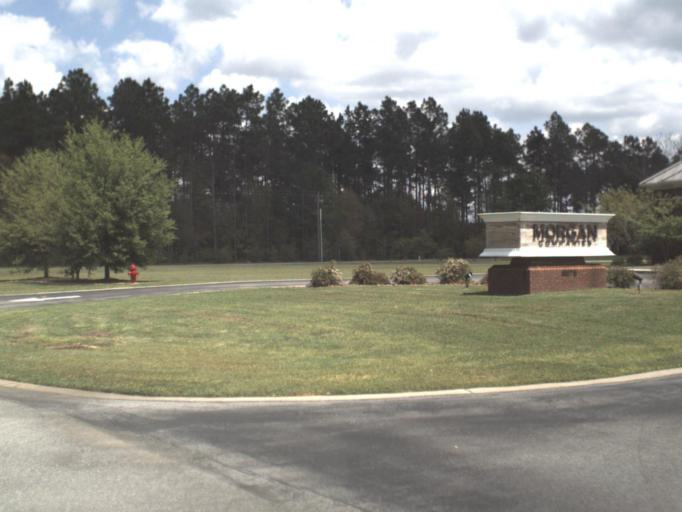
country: US
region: Florida
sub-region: Okaloosa County
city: Crestview
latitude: 30.8539
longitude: -86.6750
